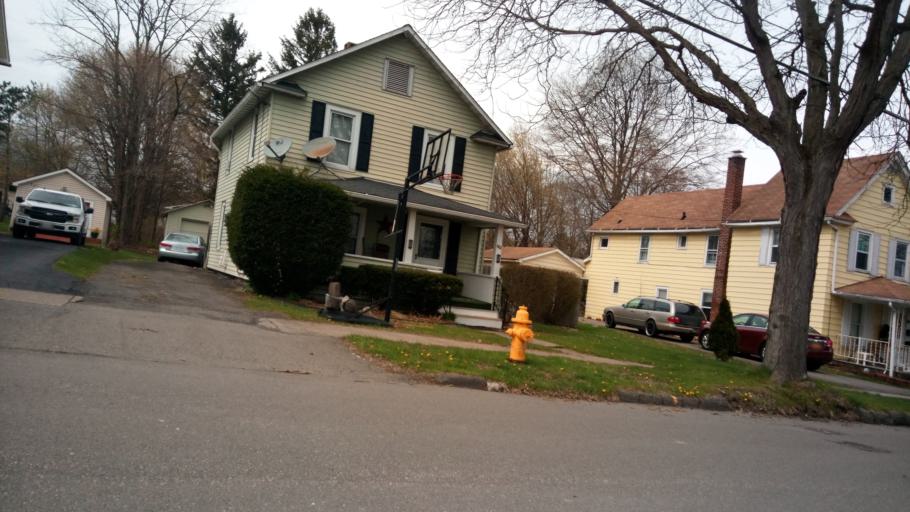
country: US
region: New York
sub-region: Chemung County
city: Elmira
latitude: 42.1022
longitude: -76.8288
